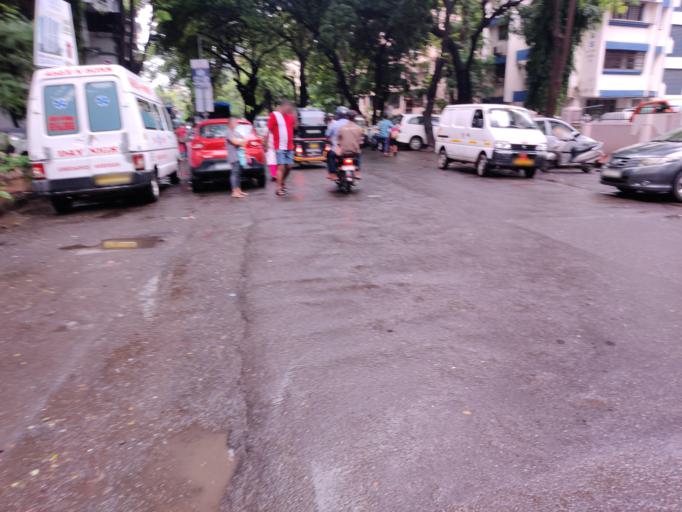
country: IN
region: Maharashtra
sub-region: Mumbai Suburban
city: Borivli
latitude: 19.2478
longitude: 72.8528
